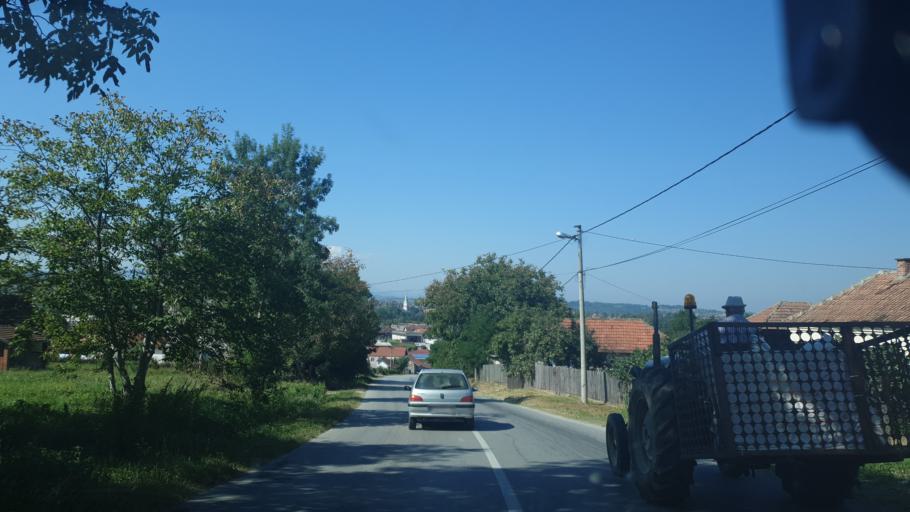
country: RS
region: Central Serbia
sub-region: Kolubarski Okrug
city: Mionica
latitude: 44.2556
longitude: 20.0975
